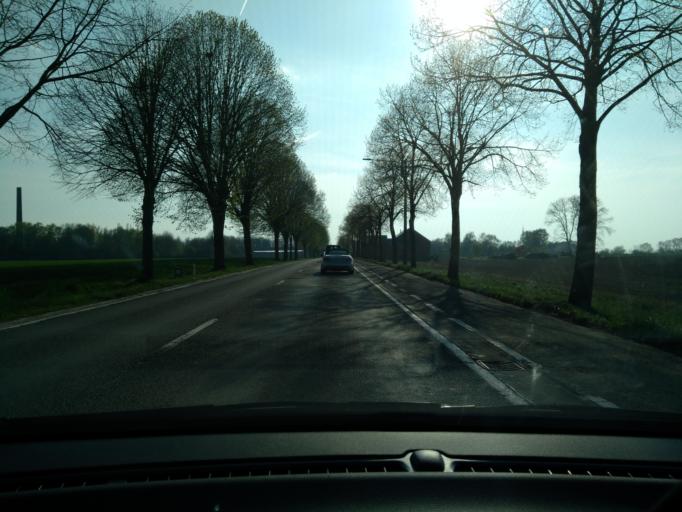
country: BE
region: Wallonia
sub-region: Province du Hainaut
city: Morlanwelz-Mariemont
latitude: 50.4436
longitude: 4.2258
